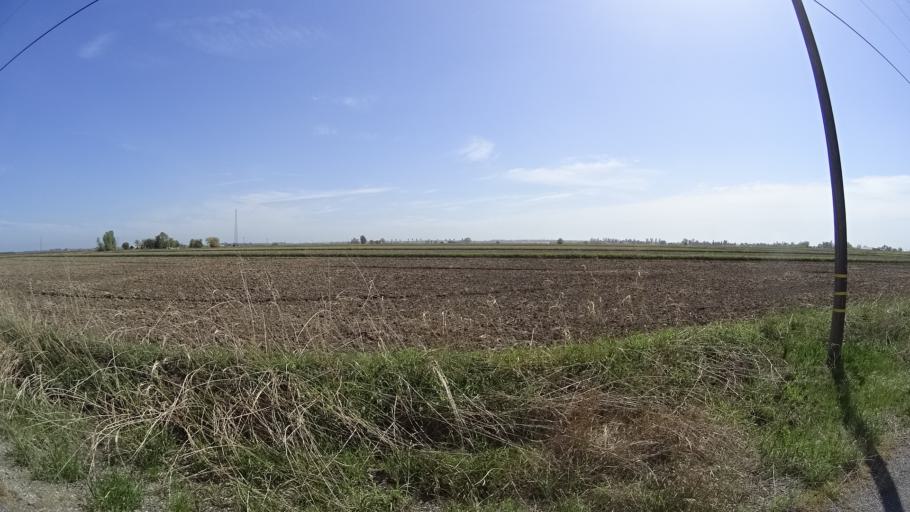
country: US
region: California
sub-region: Glenn County
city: Willows
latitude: 39.5922
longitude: -122.0558
